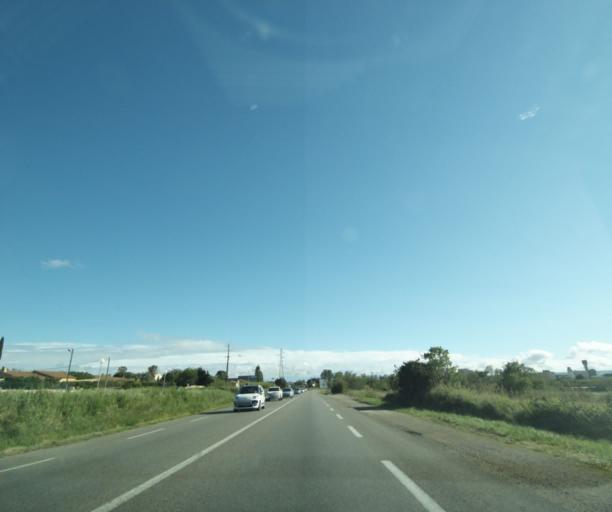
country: FR
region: Provence-Alpes-Cote d'Azur
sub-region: Departement des Bouches-du-Rhone
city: Vitrolles
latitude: 43.4510
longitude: 5.2310
